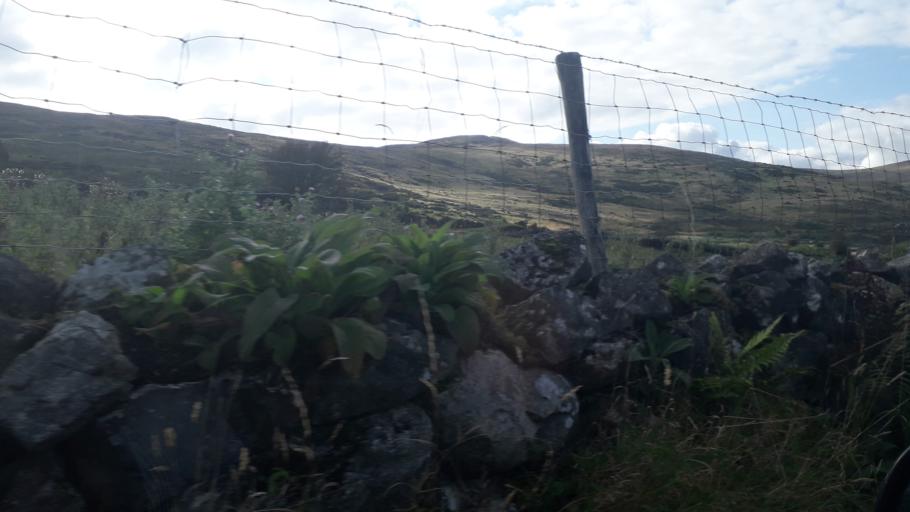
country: GB
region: Northern Ireland
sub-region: Down District
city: Warrenpoint
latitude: 54.0659
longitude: -6.2754
